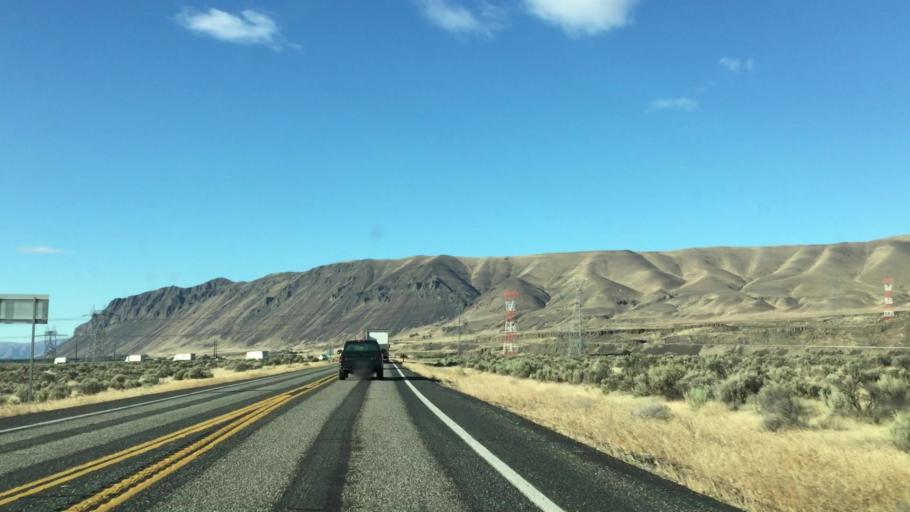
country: US
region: Washington
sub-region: Grant County
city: Mattawa
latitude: 46.8740
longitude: -119.9561
